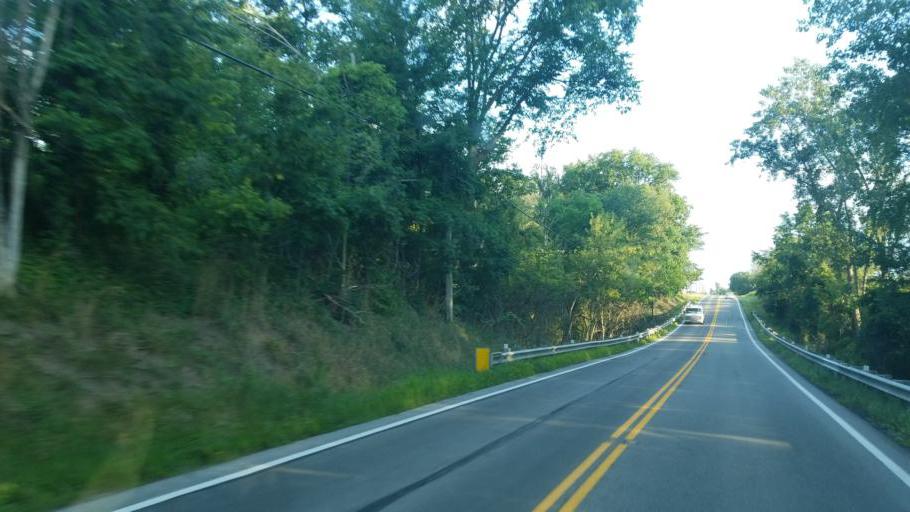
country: US
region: Ohio
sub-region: Huron County
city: Willard
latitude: 41.0771
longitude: -82.7177
